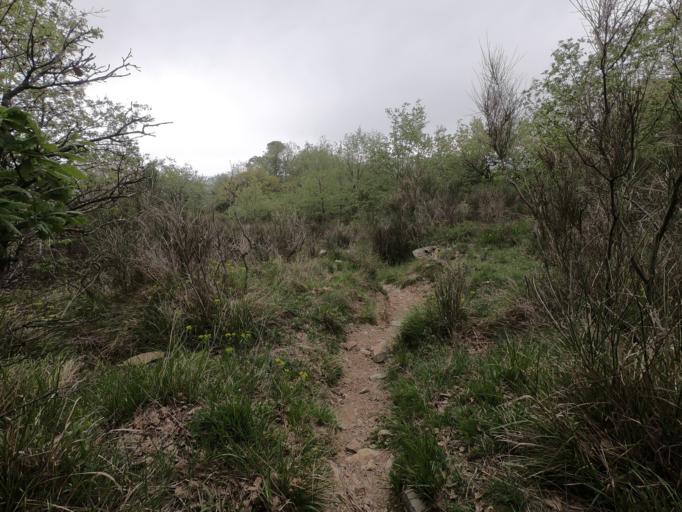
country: IT
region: Liguria
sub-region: Provincia di Imperia
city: Villa Faraldi
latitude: 43.9731
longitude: 8.0881
